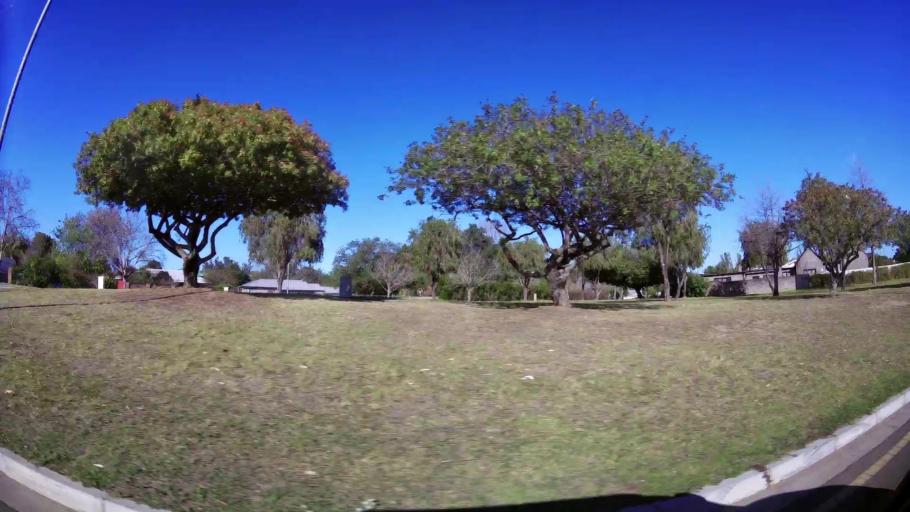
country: ZA
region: Western Cape
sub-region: Eden District Municipality
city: George
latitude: -33.9522
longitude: 22.4248
